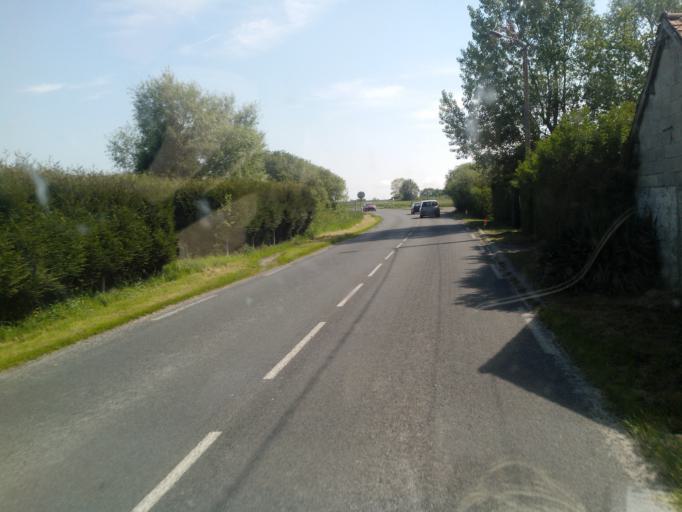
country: FR
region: Picardie
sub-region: Departement de la Somme
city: Quend
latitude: 50.3362
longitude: 1.6441
